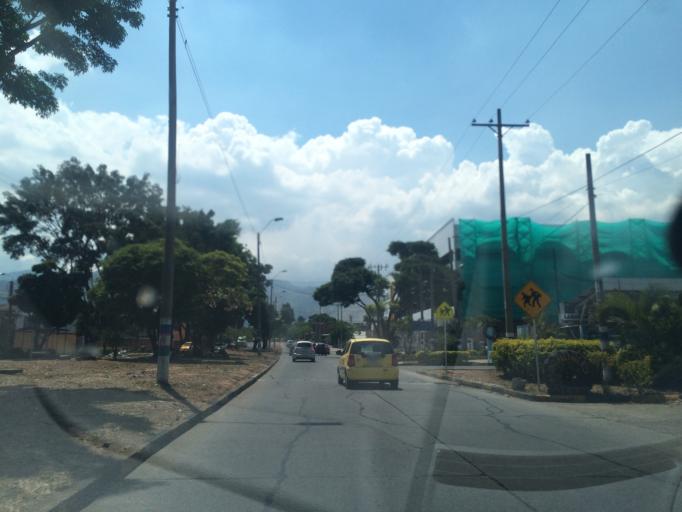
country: CO
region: Valle del Cauca
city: Cali
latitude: 3.4797
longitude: -76.5075
